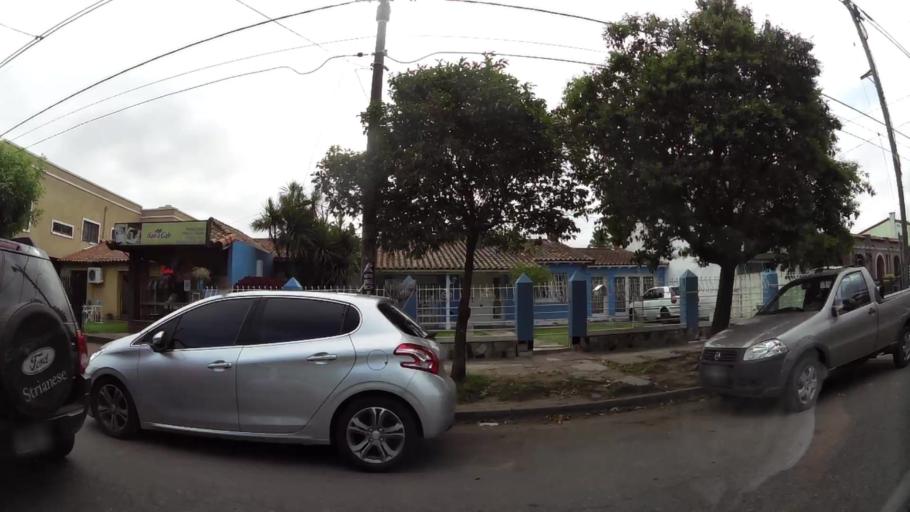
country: AR
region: Buenos Aires
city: San Justo
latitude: -34.7281
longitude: -58.5343
